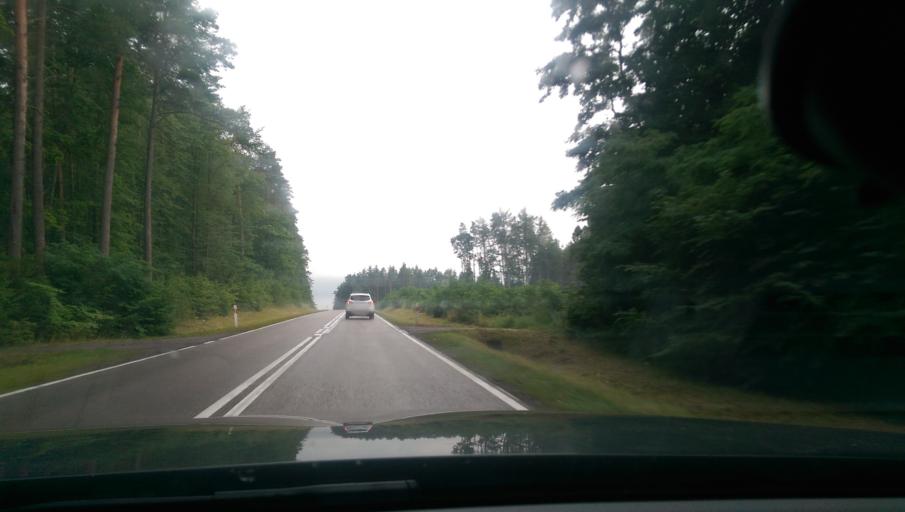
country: PL
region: Warmian-Masurian Voivodeship
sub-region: Powiat szczycienski
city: Szczytno
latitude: 53.5098
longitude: 20.9717
